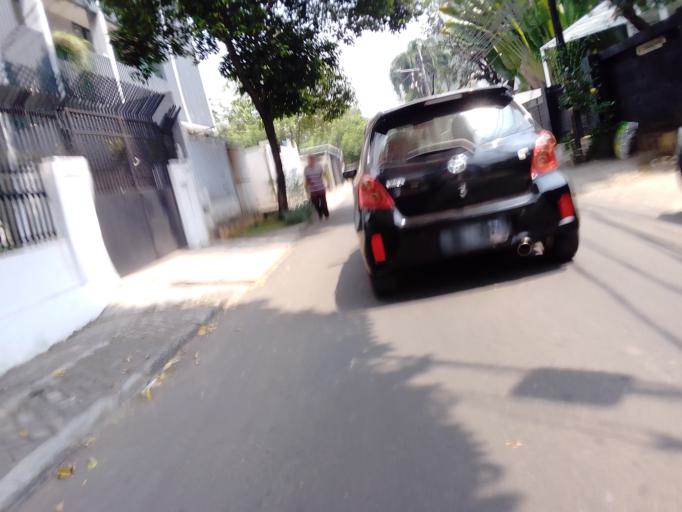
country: ID
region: Jakarta Raya
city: Jakarta
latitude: -6.2307
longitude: 106.8118
